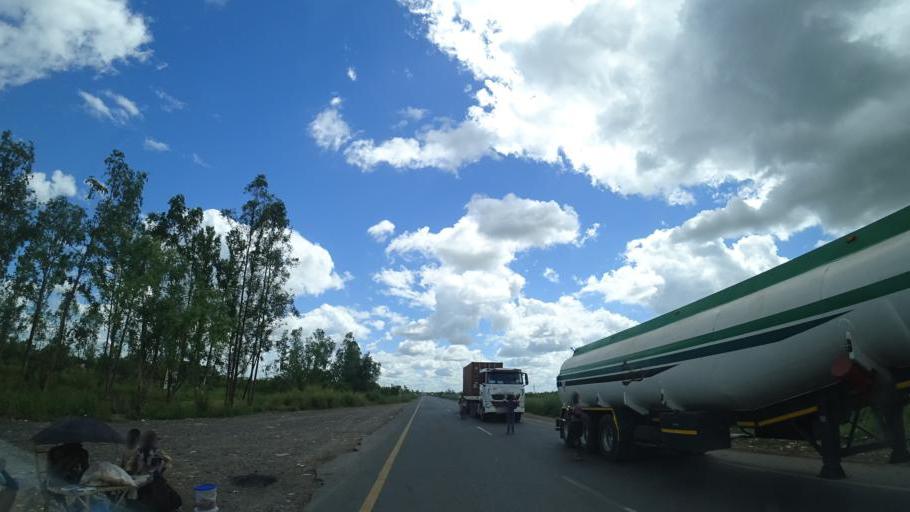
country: MZ
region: Sofala
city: Dondo
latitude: -19.2851
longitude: 34.2252
